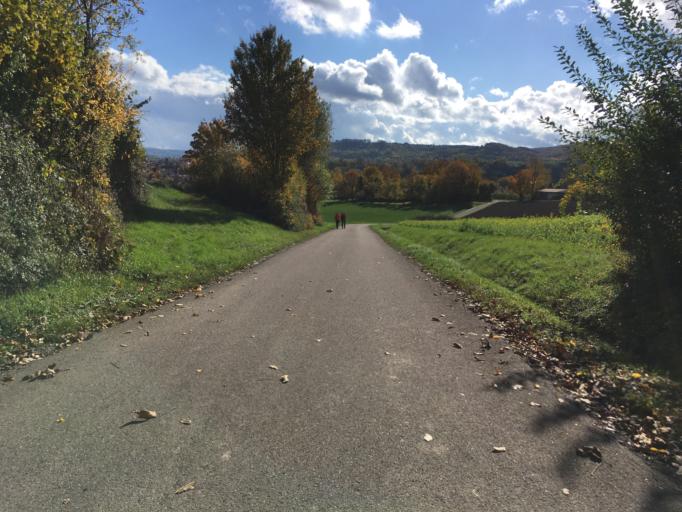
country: DE
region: Baden-Wuerttemberg
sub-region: Regierungsbezirk Stuttgart
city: Pfedelbach
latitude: 49.1860
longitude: 9.4809
